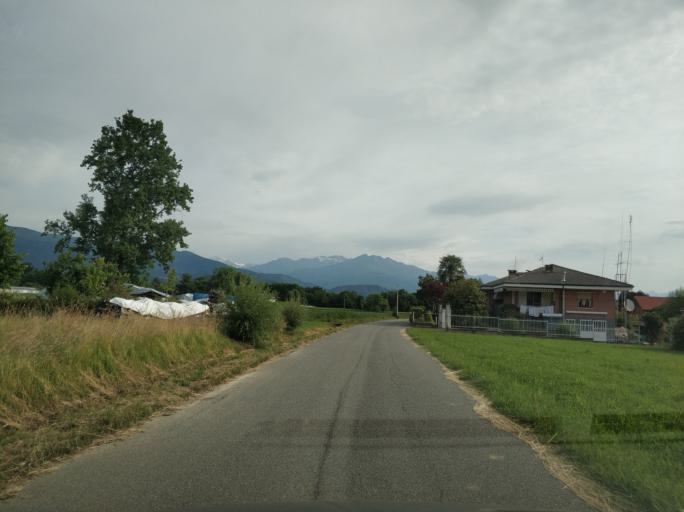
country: IT
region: Piedmont
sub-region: Provincia di Torino
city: Vauda Canavese Superiore
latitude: 45.2905
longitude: 7.6222
